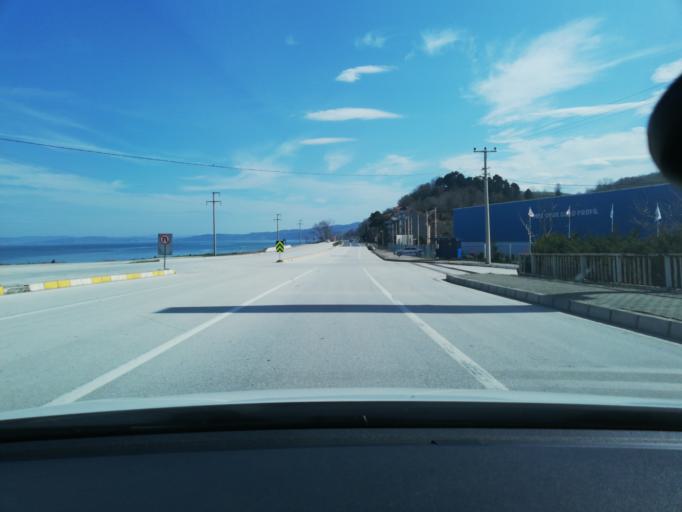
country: TR
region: Duzce
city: Akcakoca
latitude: 41.0950
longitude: 31.1963
